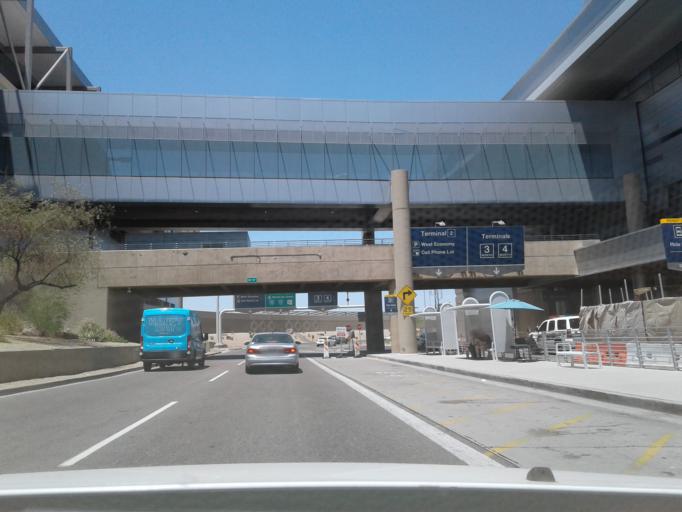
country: US
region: Arizona
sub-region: Maricopa County
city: Phoenix
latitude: 33.4347
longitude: -112.0091
